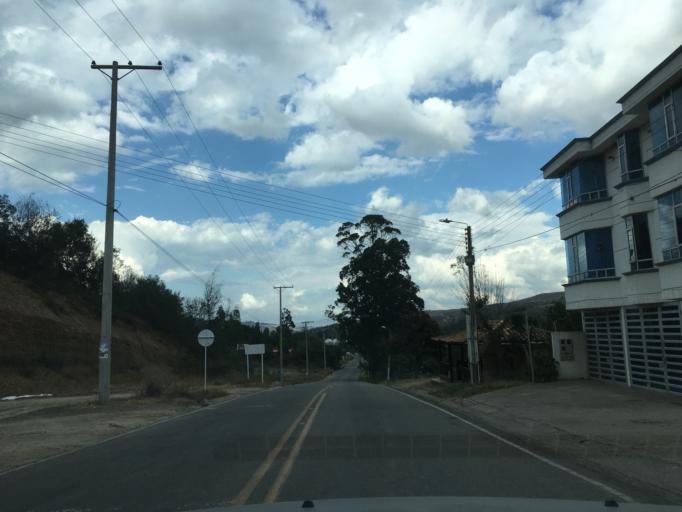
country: CO
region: Boyaca
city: Sutamarchan
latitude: 5.5819
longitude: -73.6445
